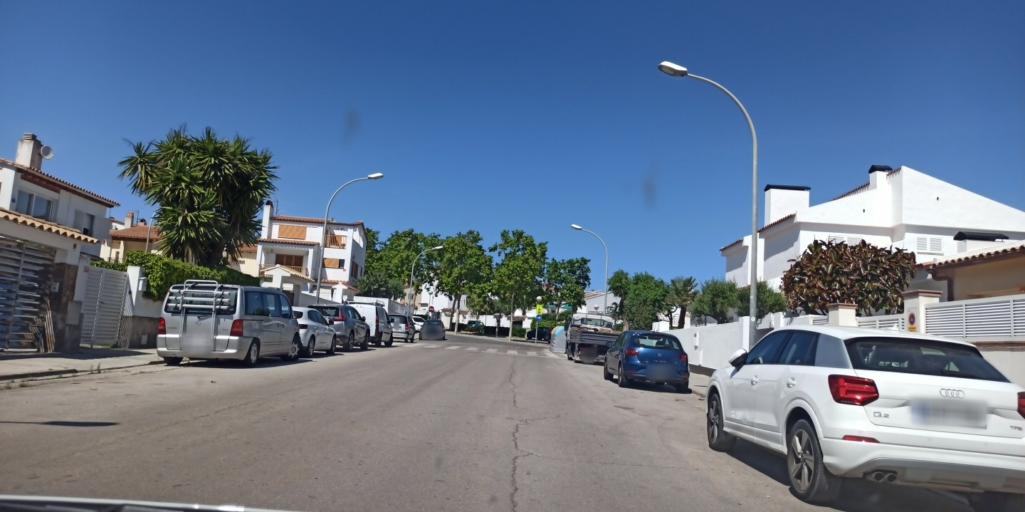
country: ES
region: Catalonia
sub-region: Provincia de Barcelona
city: Sant Pere de Ribes
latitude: 41.2585
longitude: 1.7799
